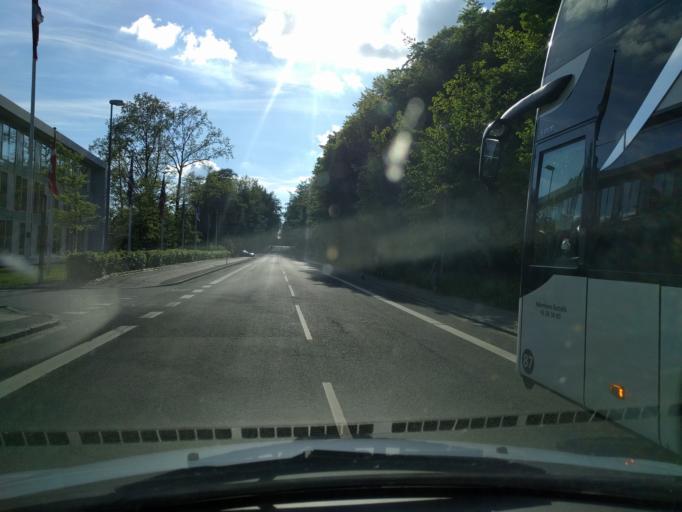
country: DK
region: South Denmark
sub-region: Nyborg Kommune
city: Nyborg
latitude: 55.3185
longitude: 10.8106
